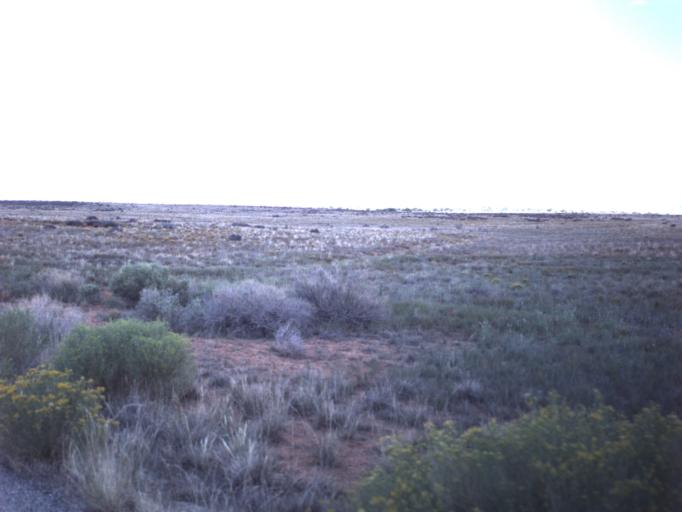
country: US
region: Utah
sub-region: Grand County
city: Moab
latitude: 38.4975
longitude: -109.7336
